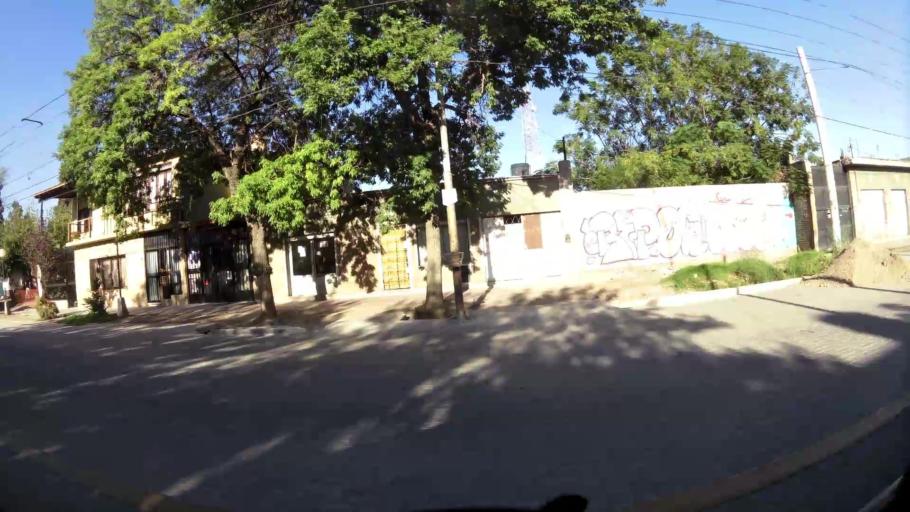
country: AR
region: Mendoza
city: Las Heras
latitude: -32.8546
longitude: -68.8340
